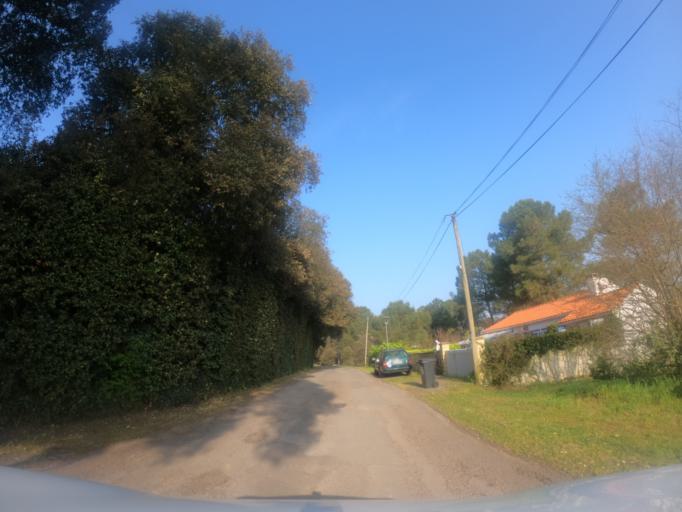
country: FR
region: Pays de la Loire
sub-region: Departement de la Vendee
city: La Tranche-sur-Mer
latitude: 46.3477
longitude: -1.4495
